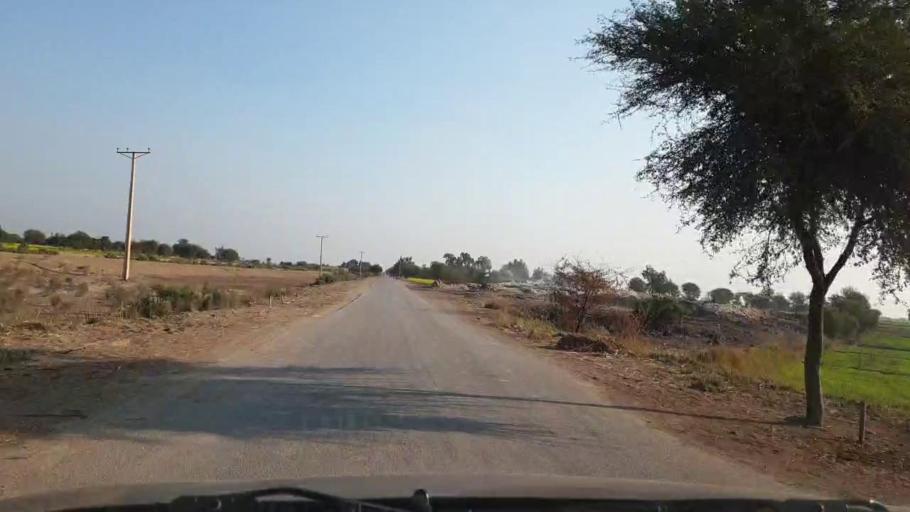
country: PK
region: Sindh
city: Jhol
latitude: 25.9561
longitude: 68.8975
